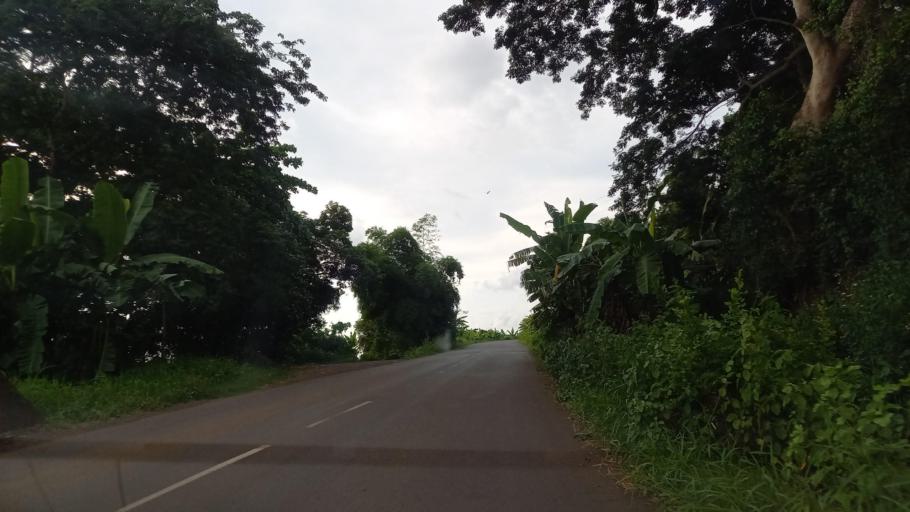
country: YT
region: M'Tsangamouji
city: M'Tsangamouji
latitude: -12.7613
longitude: 45.0722
